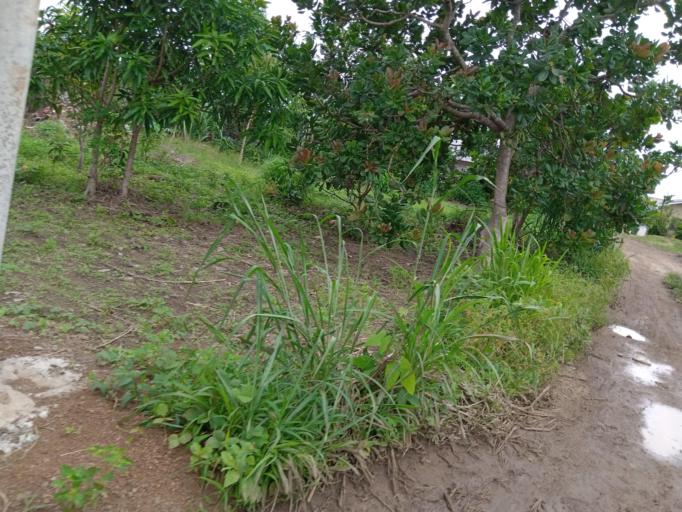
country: SL
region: Southern Province
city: Moyamba
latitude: 8.1689
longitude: -12.4220
